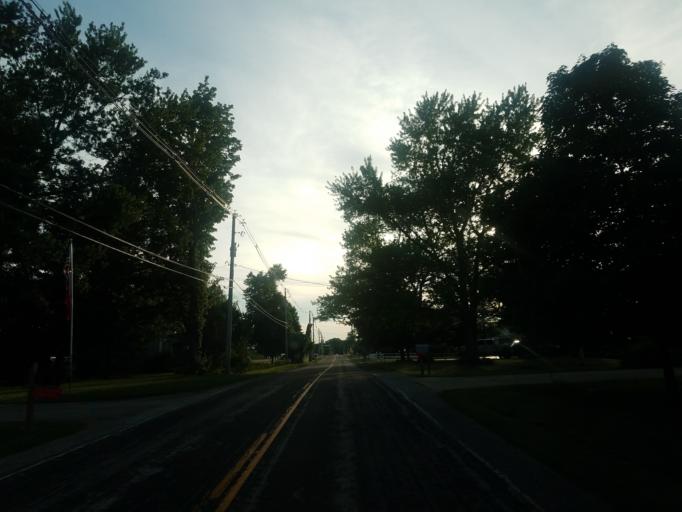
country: US
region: Illinois
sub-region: McLean County
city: Bloomington
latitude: 40.4442
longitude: -88.9862
